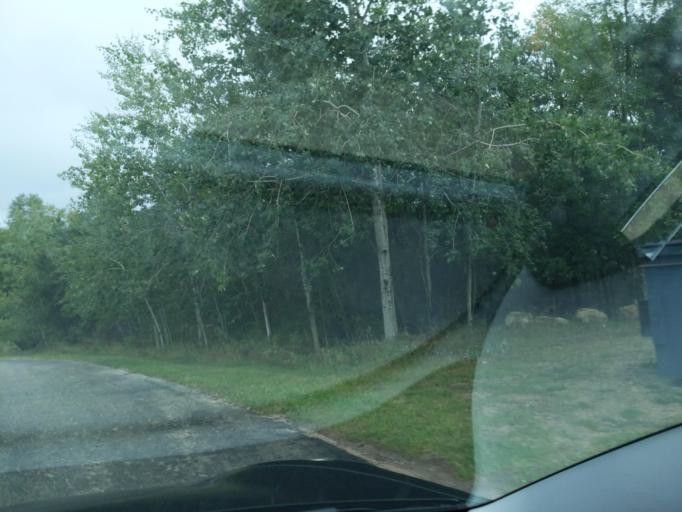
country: US
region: Michigan
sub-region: Antrim County
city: Elk Rapids
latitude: 44.8160
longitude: -85.3878
